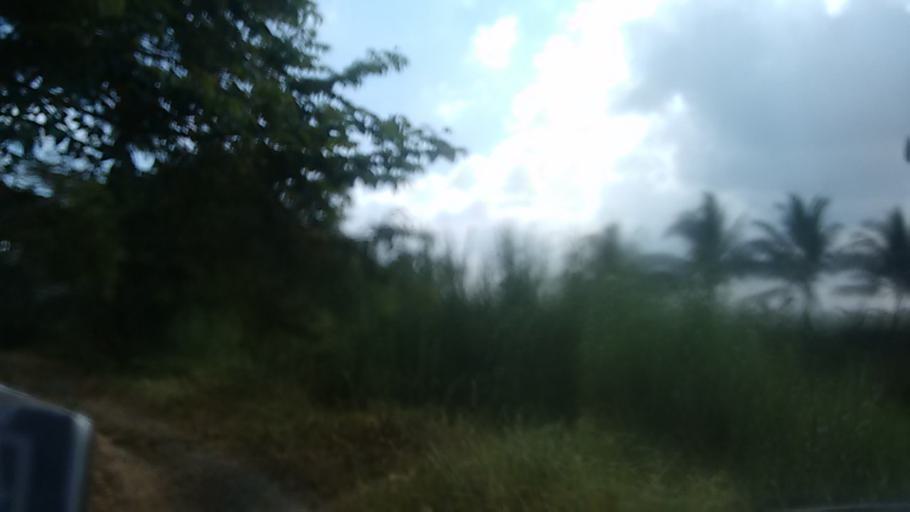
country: IN
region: Kerala
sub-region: Thrissur District
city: Trichur
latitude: 10.5303
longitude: 76.1465
